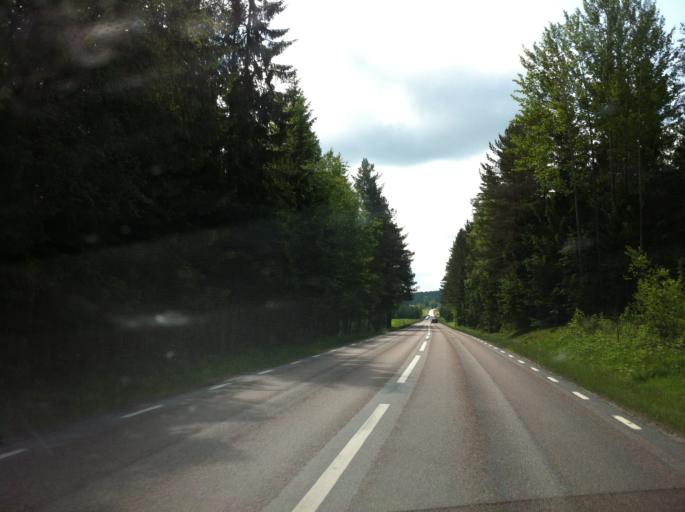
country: SE
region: Vaermland
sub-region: Karlstads Kommun
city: Edsvalla
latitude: 59.6116
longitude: 13.1538
